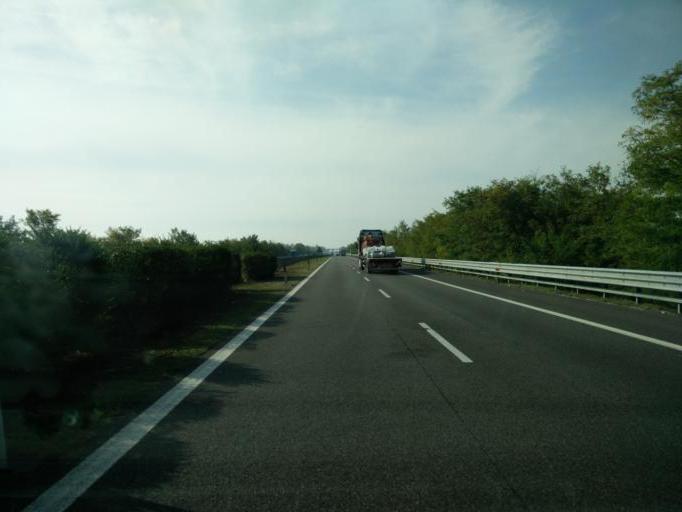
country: IT
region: Lombardy
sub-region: Provincia di Brescia
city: Alfianello
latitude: 45.2504
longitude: 10.1222
